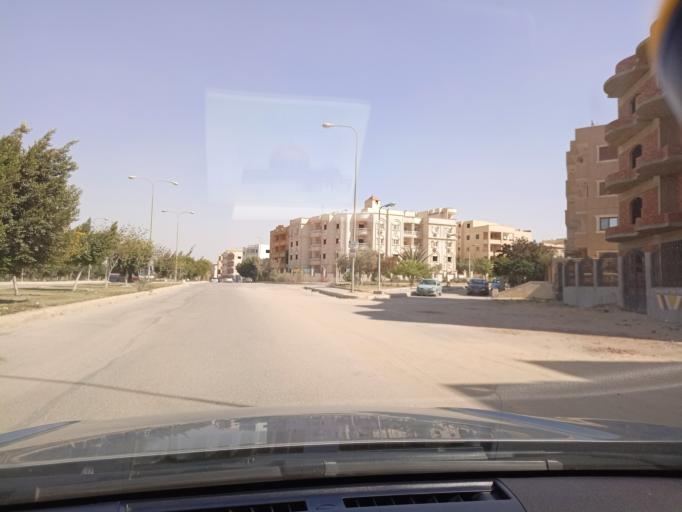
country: EG
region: Muhafazat al Qalyubiyah
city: Al Khankah
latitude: 30.2285
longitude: 31.4448
